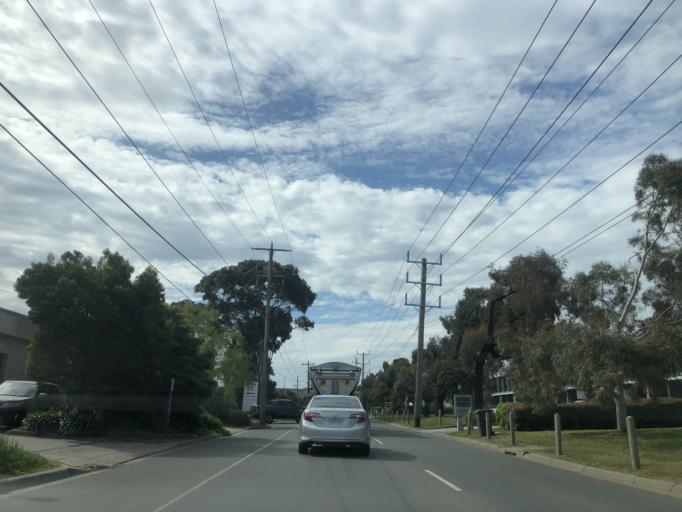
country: AU
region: Victoria
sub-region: Monash
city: Notting Hill
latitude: -37.9192
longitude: 145.1467
